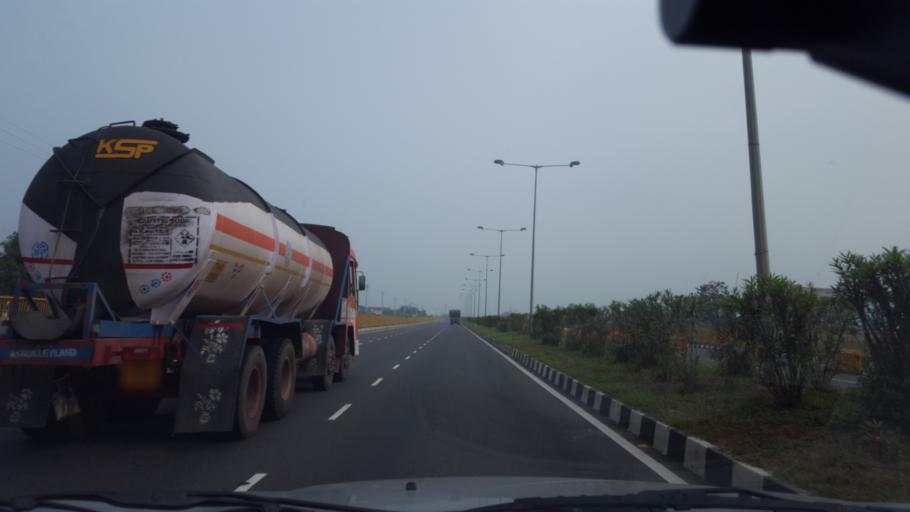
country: IN
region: Andhra Pradesh
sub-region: Guntur
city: Chilakalurupet
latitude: 16.0021
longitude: 80.1122
